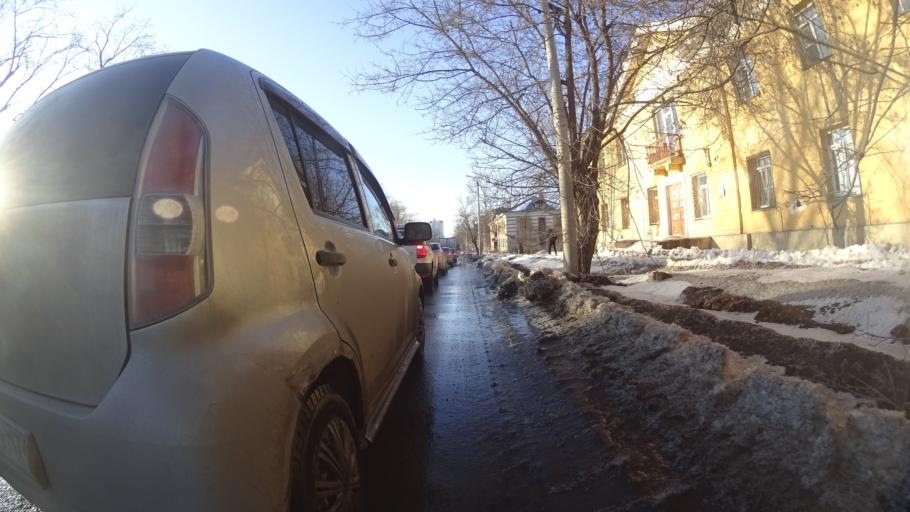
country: RU
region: Chelyabinsk
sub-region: Gorod Chelyabinsk
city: Chelyabinsk
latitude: 55.1343
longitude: 61.4588
